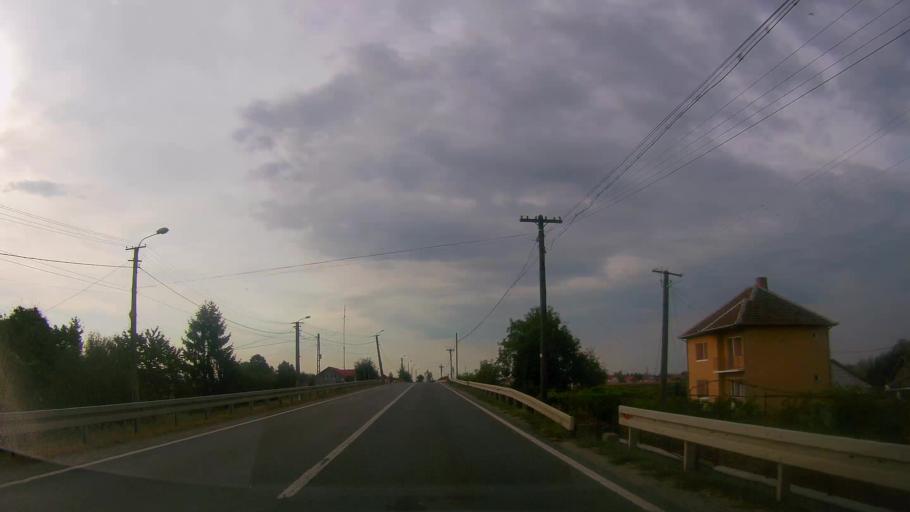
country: RO
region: Satu Mare
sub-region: Comuna Turulung
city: Turulung
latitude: 47.9300
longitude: 23.0847
